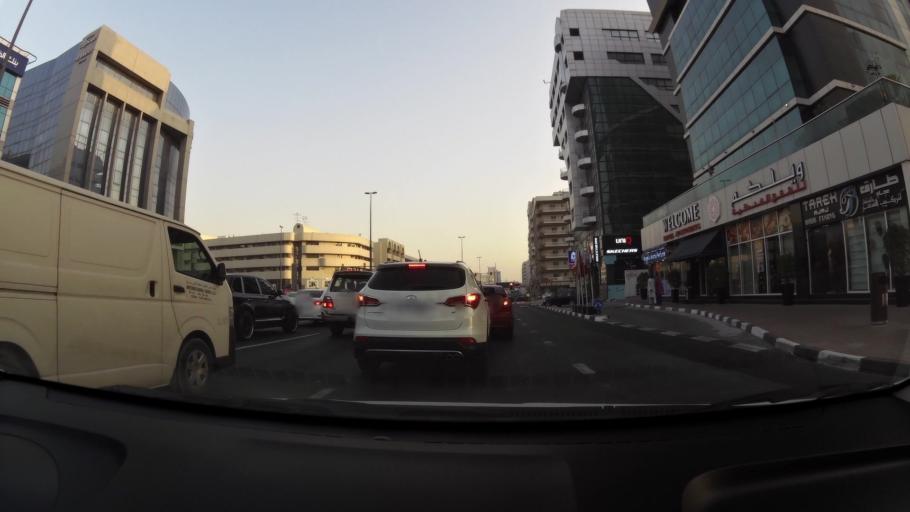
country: AE
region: Ash Shariqah
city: Sharjah
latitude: 25.2647
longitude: 55.3298
